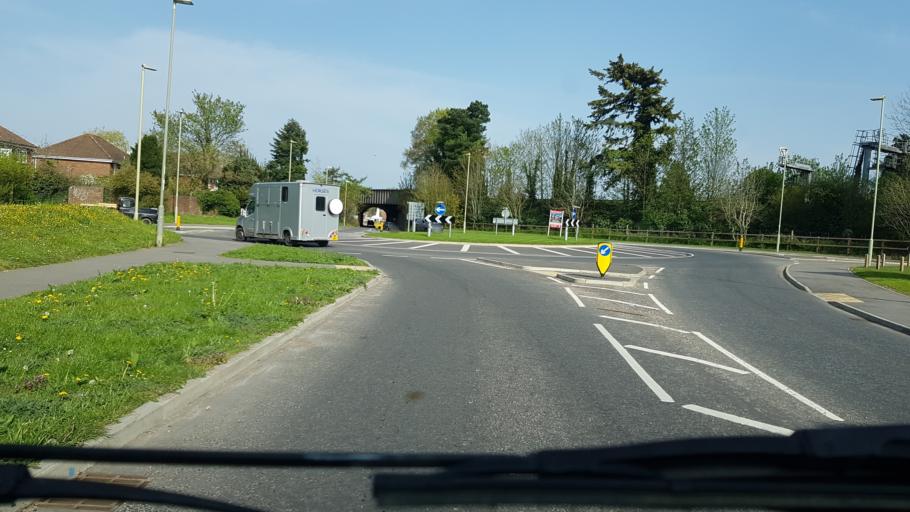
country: GB
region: England
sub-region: Hampshire
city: Basingstoke
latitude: 51.2619
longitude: -1.1381
